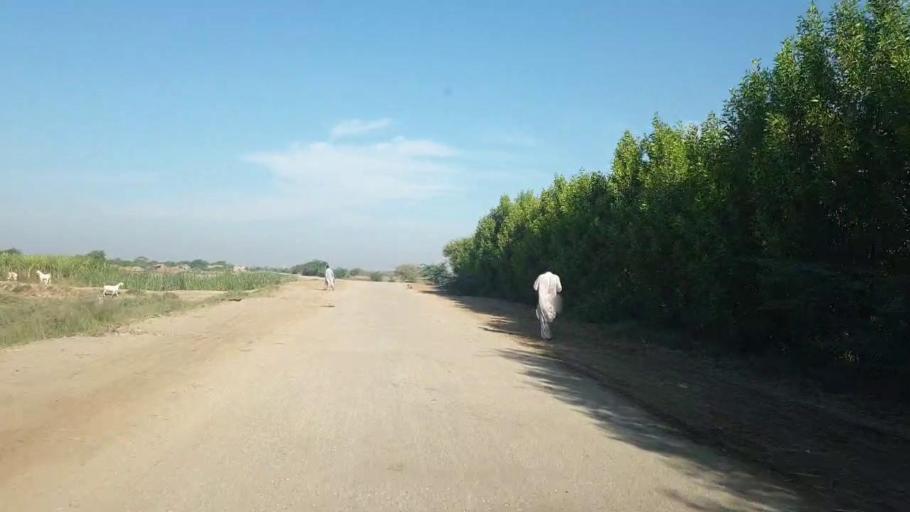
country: PK
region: Sindh
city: Talhar
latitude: 24.9459
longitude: 68.7866
